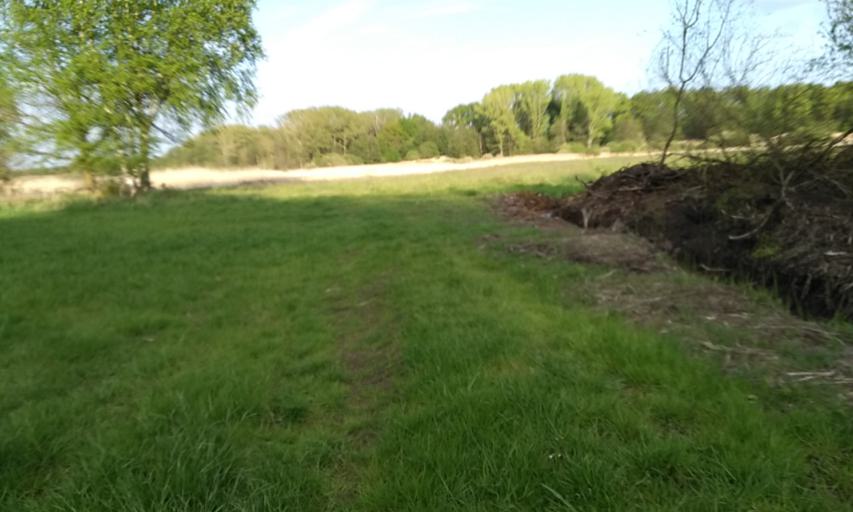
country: DE
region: Lower Saxony
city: Bliedersdorf
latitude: 53.4875
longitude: 9.5464
